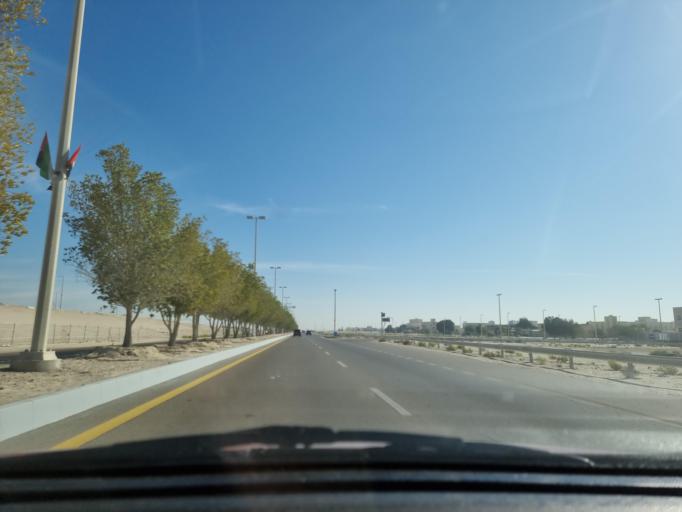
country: AE
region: Abu Dhabi
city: Abu Dhabi
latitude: 24.3999
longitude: 54.7085
